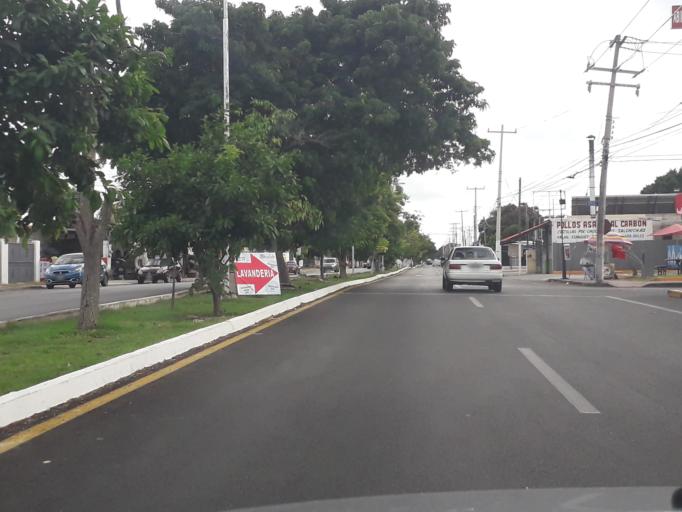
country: MX
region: Yucatan
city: Merida
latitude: 20.9711
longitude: -89.6636
